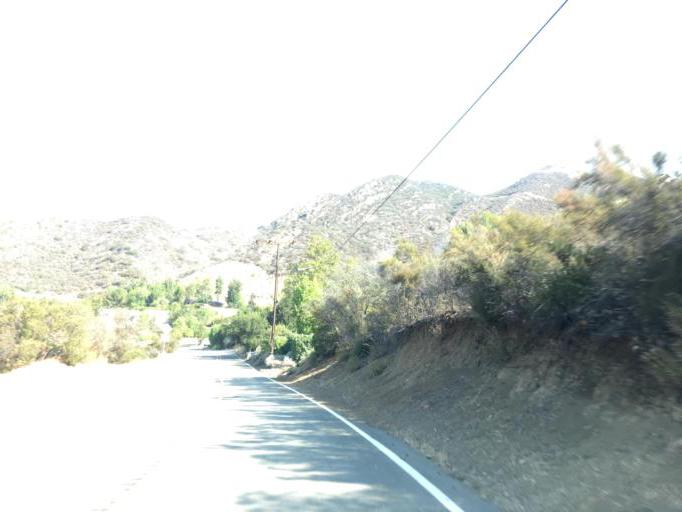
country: US
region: California
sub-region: Los Angeles County
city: Topanga
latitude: 34.0998
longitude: -118.6537
